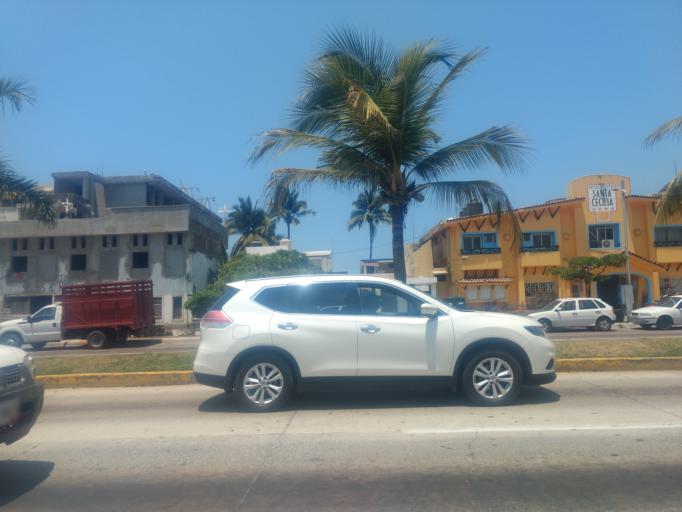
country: MX
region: Colima
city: Tapeixtles
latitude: 19.0901
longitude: -104.3135
